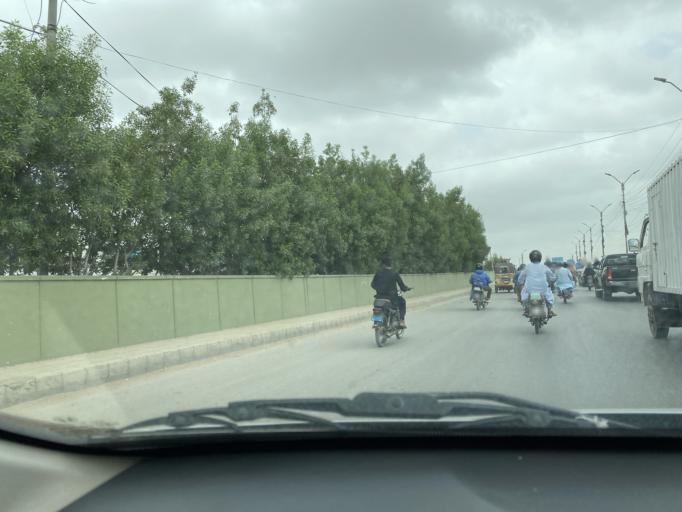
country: PK
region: Sindh
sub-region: Karachi District
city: Karachi
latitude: 24.8643
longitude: 67.0855
